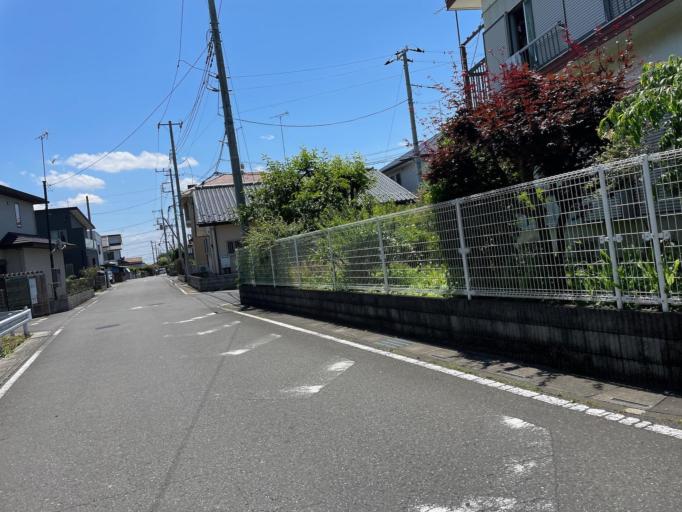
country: JP
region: Saitama
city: Sakado
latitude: 36.0031
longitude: 139.4039
